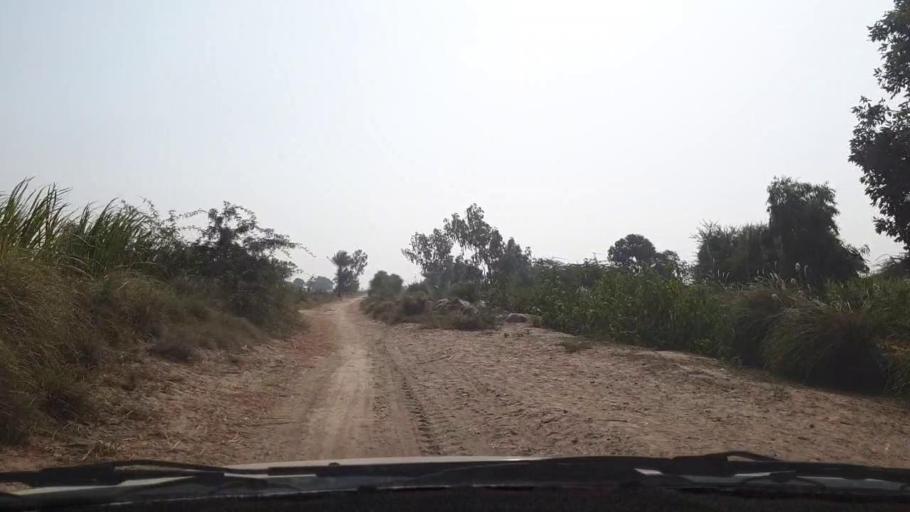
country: PK
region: Sindh
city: Tando Muhammad Khan
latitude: 25.0777
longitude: 68.3619
